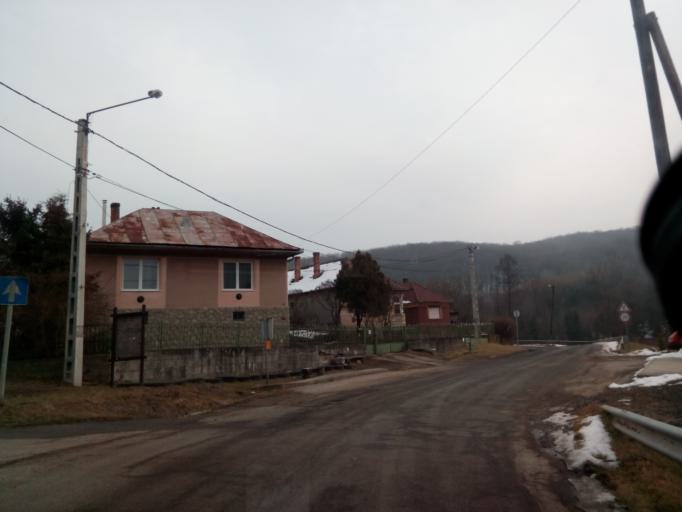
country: HU
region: Borsod-Abauj-Zemplen
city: Gonc
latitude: 48.4846
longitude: 21.3659
